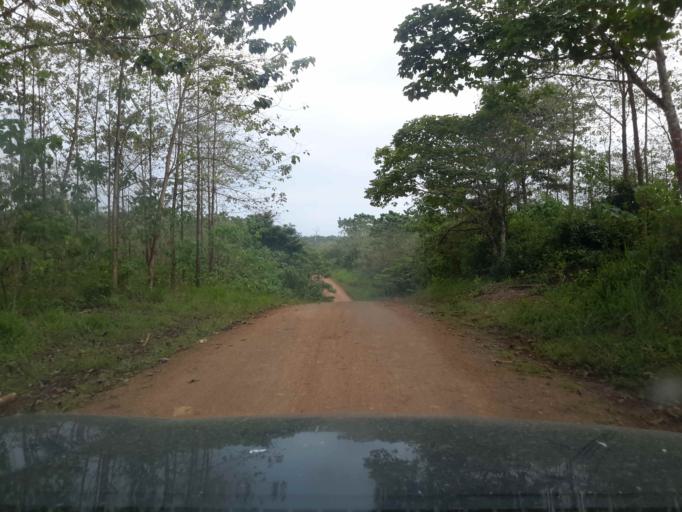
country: CR
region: Alajuela
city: Los Chiles
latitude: 11.0603
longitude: -84.4877
